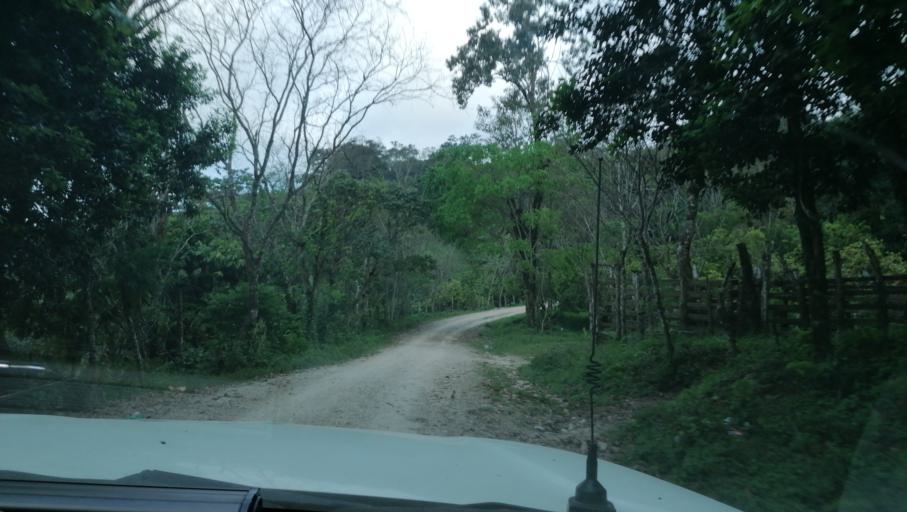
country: MX
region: Chiapas
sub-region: Francisco Leon
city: San Miguel la Sardina
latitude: 17.3102
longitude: -93.2676
